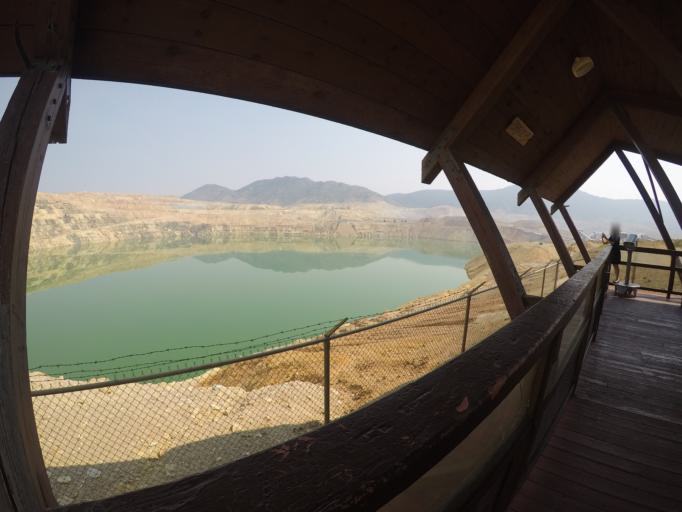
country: US
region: Montana
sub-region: Silver Bow County
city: Butte
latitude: 46.0119
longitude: -112.5178
